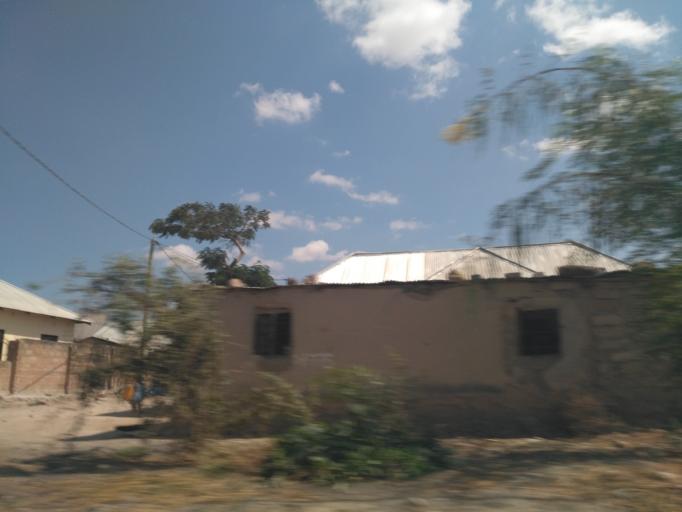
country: TZ
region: Dodoma
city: Dodoma
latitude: -6.1498
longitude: 35.7320
